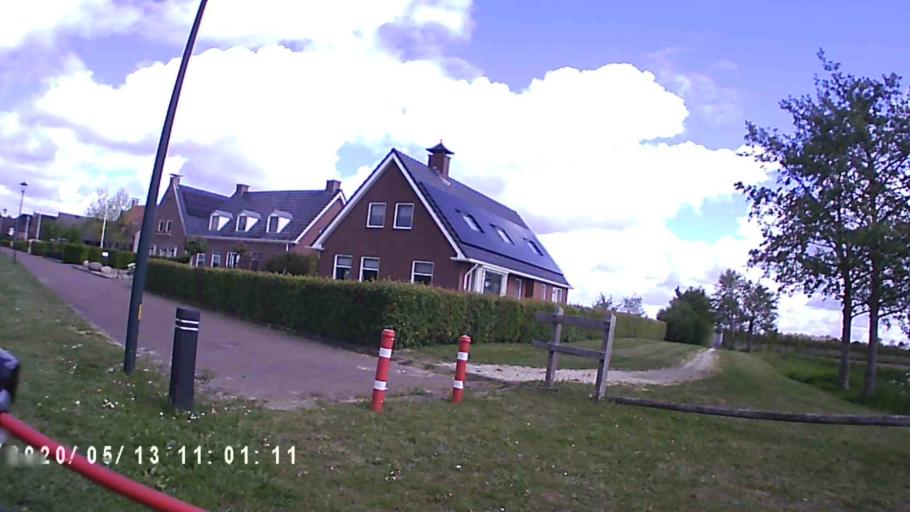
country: NL
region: Groningen
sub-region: Gemeente Zuidhorn
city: Grijpskerk
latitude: 53.2830
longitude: 6.3270
